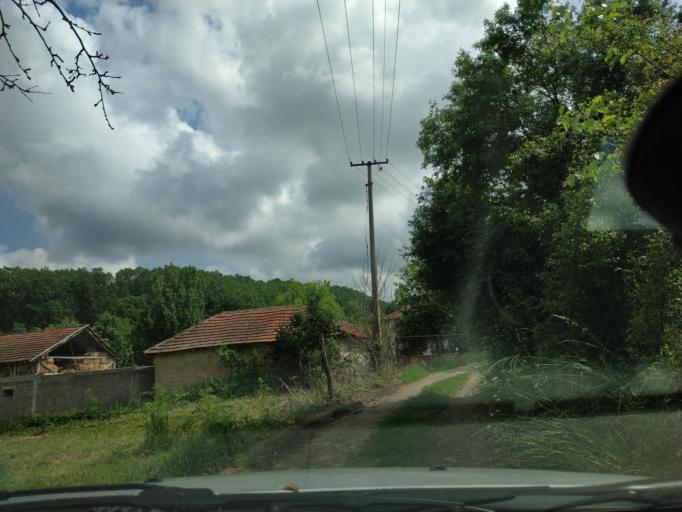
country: RS
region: Central Serbia
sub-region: Nisavski Okrug
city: Aleksinac
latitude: 43.4242
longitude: 21.5844
